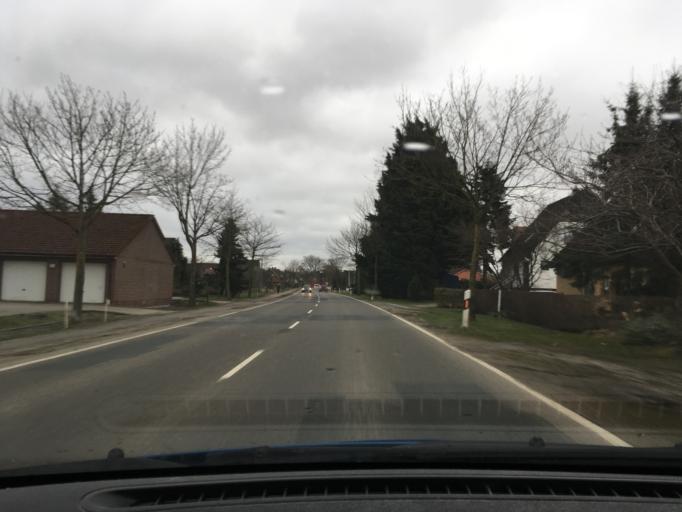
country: DE
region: Lower Saxony
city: Marschacht
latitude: 53.4212
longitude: 10.3287
